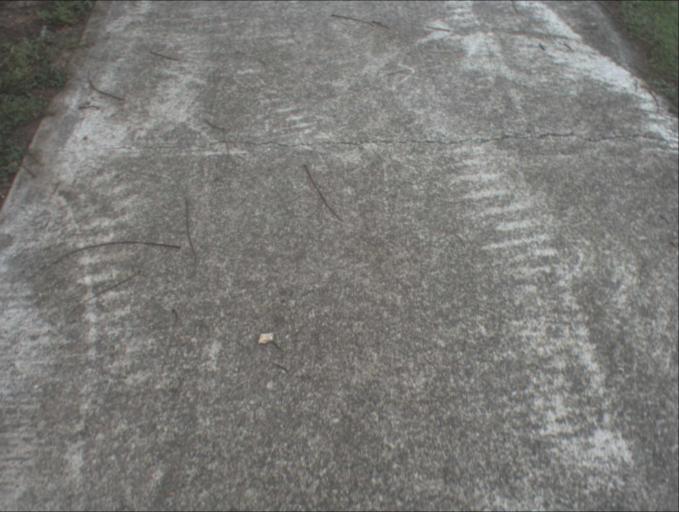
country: AU
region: Queensland
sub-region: Logan
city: Park Ridge South
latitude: -27.6865
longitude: 153.0314
